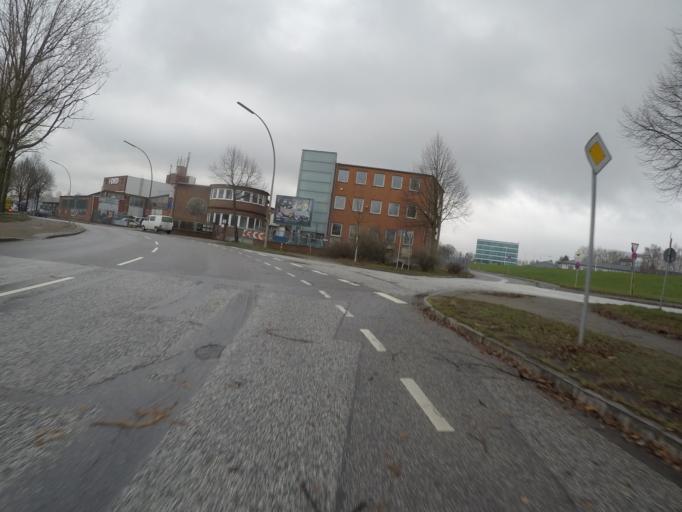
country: DE
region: Hamburg
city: Harburg
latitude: 53.4788
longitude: 9.9930
